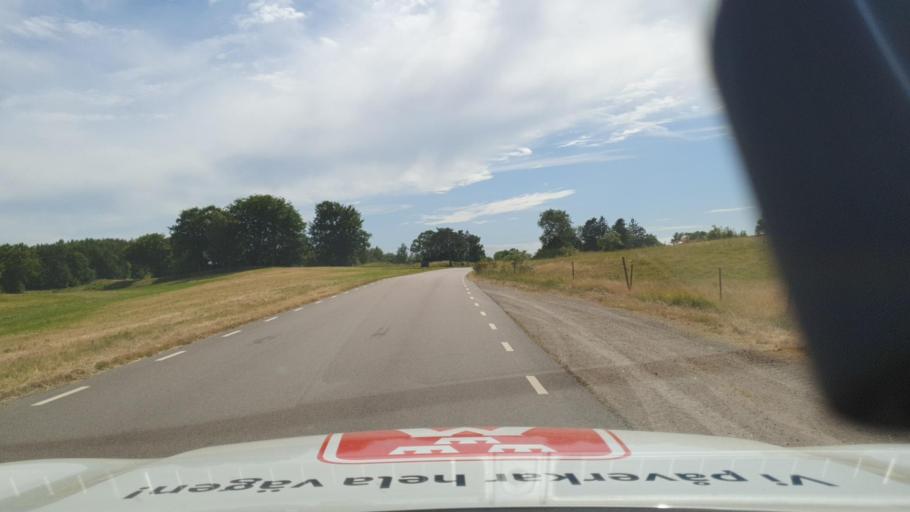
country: SE
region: Skane
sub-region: Tomelilla Kommun
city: Tomelilla
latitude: 55.6796
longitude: 13.9383
